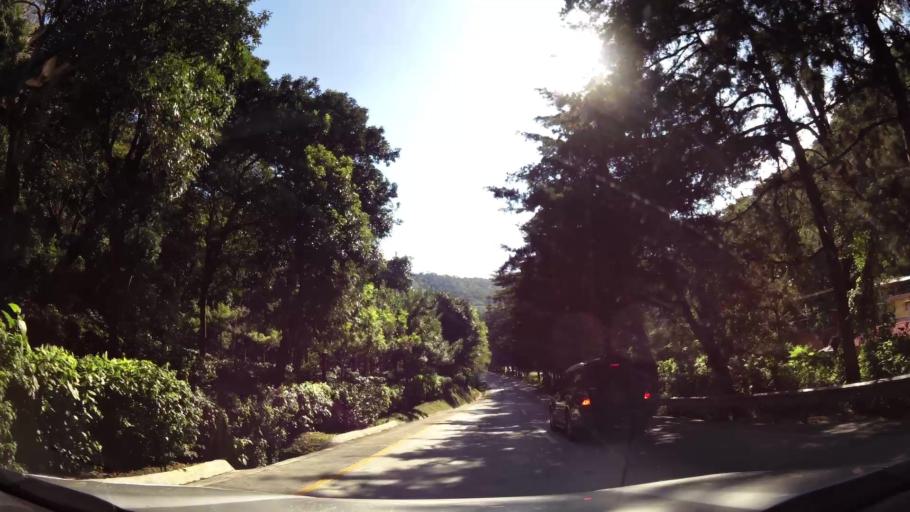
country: GT
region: Sacatepequez
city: Santa Lucia Milpas Altas
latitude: 14.5638
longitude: -90.7015
